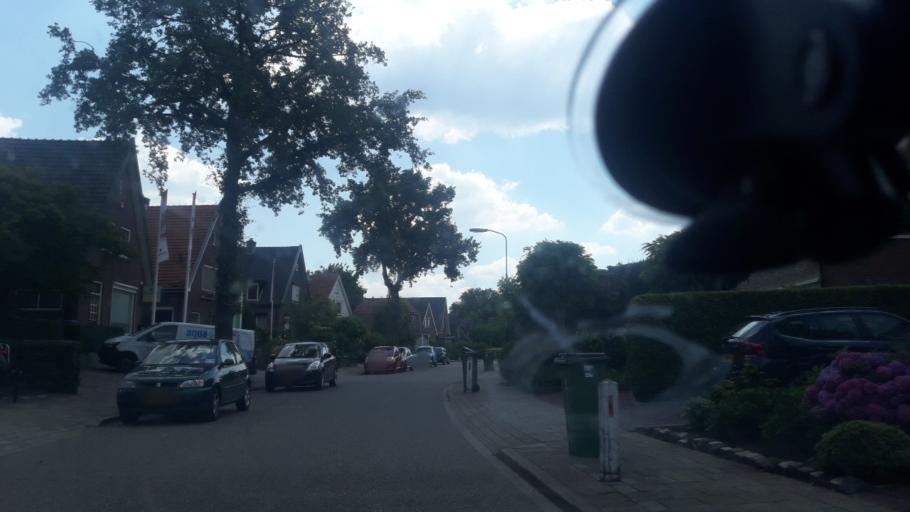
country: NL
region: Gelderland
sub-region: Gemeente Ede
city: Ede
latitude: 52.0480
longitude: 5.6559
